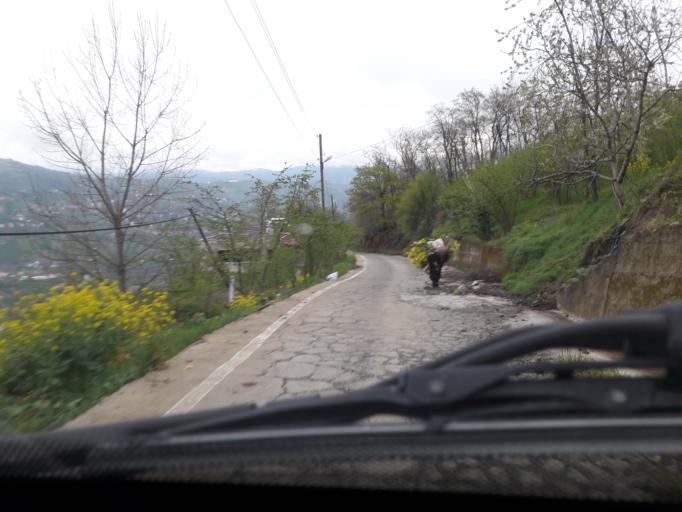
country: TR
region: Trabzon
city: Duzkoy
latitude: 40.9008
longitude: 39.4845
